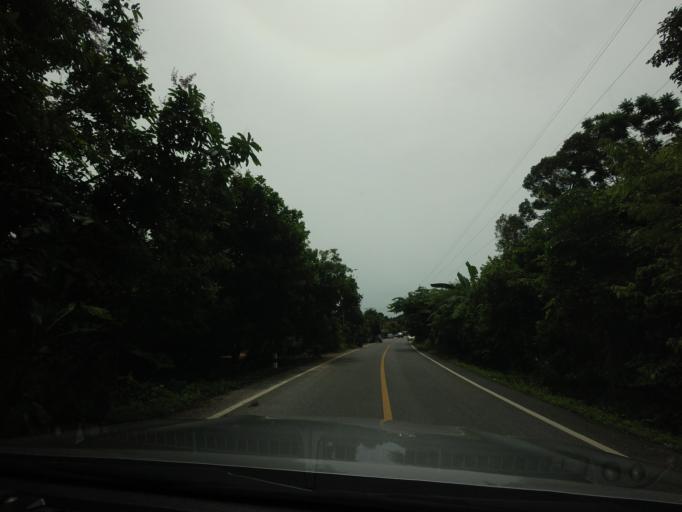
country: TH
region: Pattani
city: Kapho
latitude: 6.6065
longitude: 101.5355
